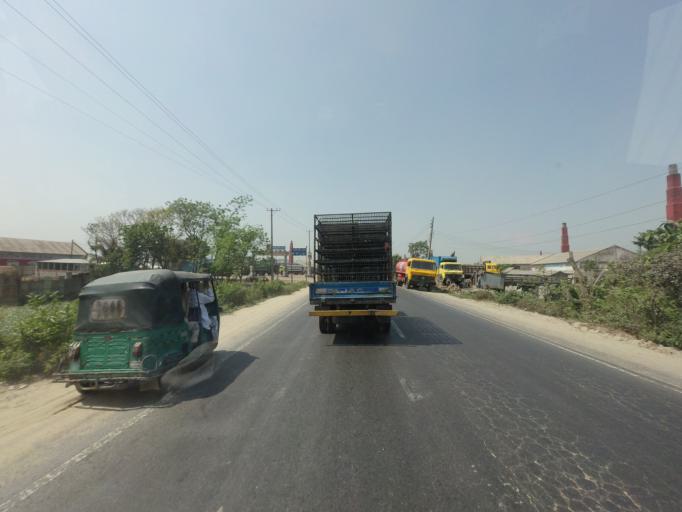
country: BD
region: Dhaka
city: Bhairab Bazar
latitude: 24.0450
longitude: 91.0695
